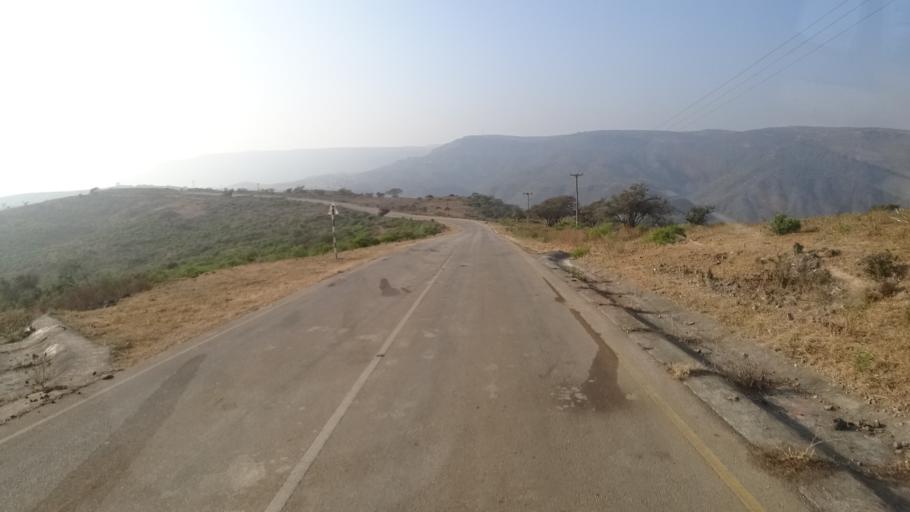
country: YE
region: Al Mahrah
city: Hawf
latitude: 16.7431
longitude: 53.3610
